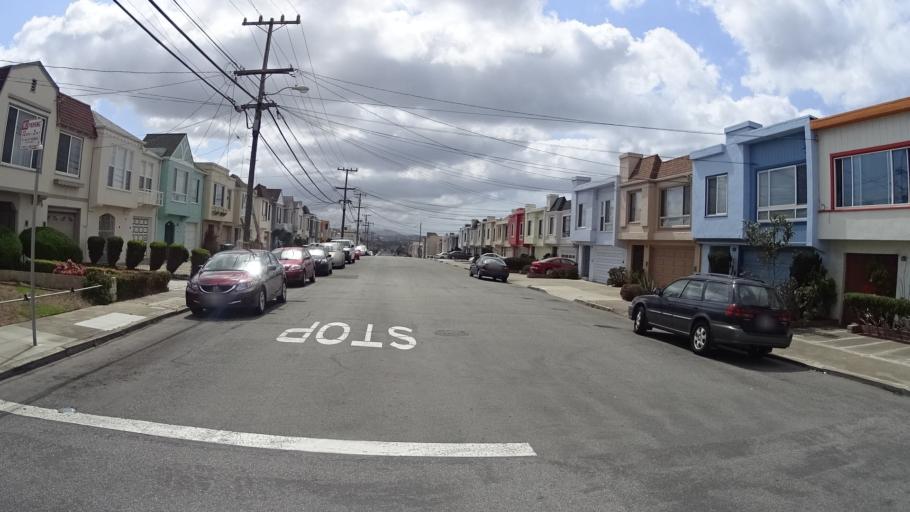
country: US
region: California
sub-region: San Mateo County
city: Daly City
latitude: 37.7439
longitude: -122.4972
